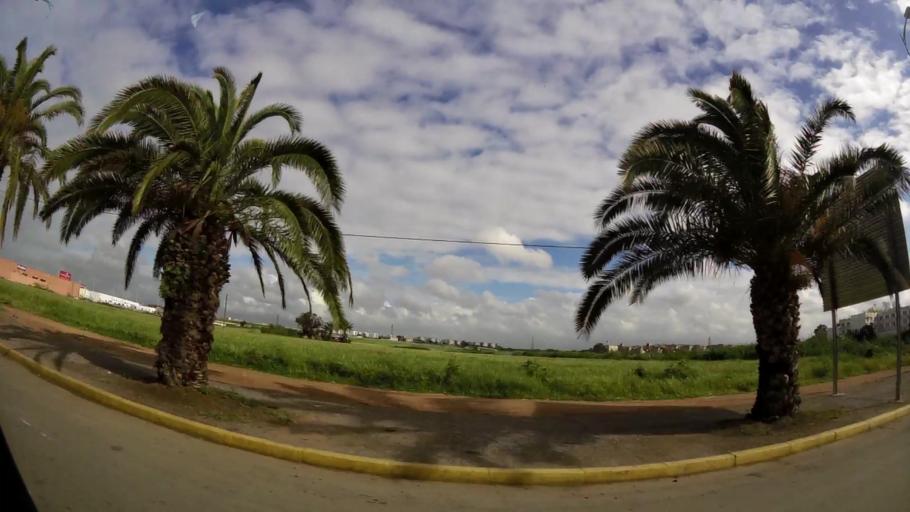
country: MA
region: Grand Casablanca
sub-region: Mohammedia
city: Mohammedia
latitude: 33.7081
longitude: -7.3520
